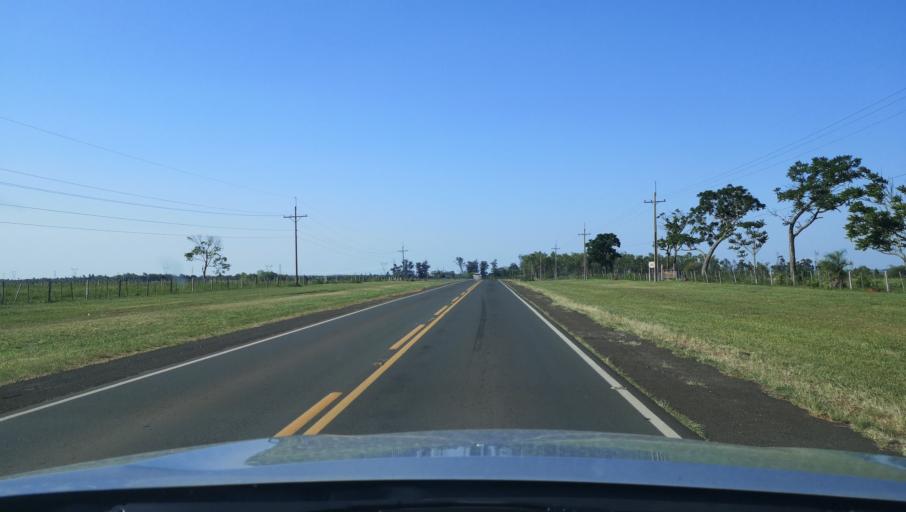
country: PY
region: Misiones
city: Santa Maria
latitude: -26.8124
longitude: -57.0223
